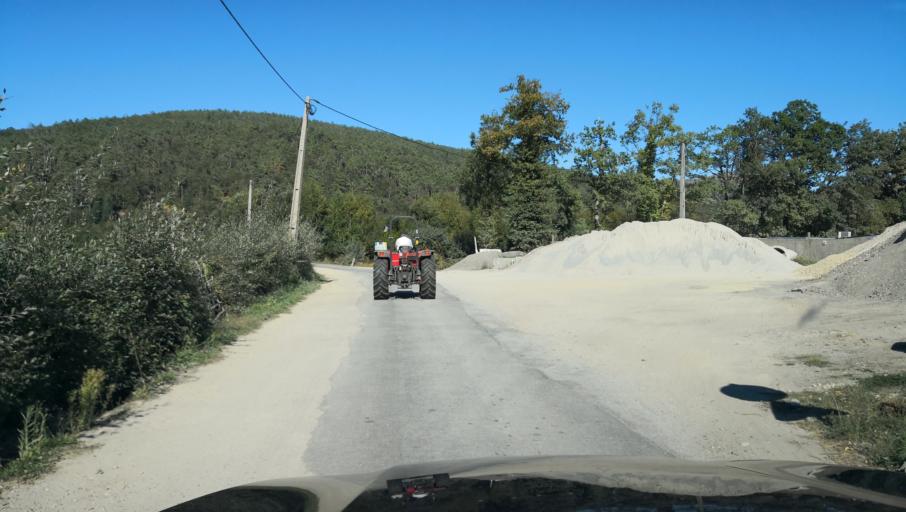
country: PT
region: Vila Real
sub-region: Santa Marta de Penaguiao
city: Santa Marta de Penaguiao
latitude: 41.2859
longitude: -7.8555
